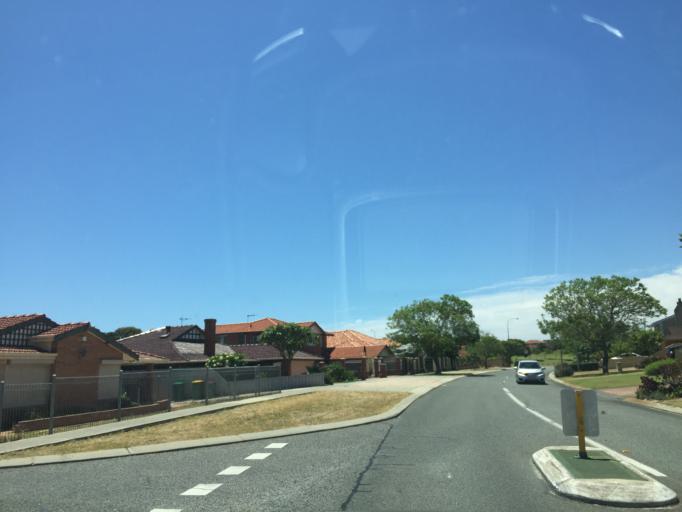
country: AU
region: Western Australia
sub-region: Melville
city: Winthrop
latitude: -32.0610
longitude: 115.8352
